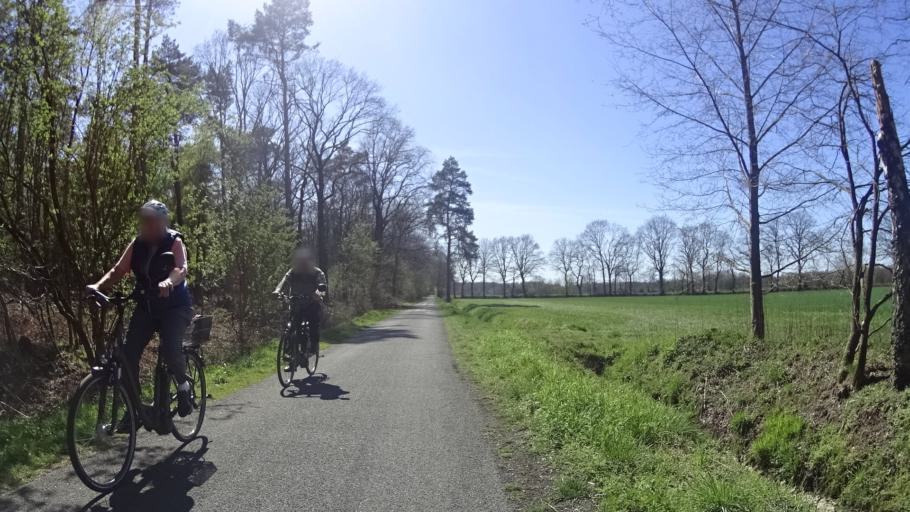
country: DE
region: North Rhine-Westphalia
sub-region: Regierungsbezirk Munster
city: Dulmen
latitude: 51.7818
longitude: 7.2484
